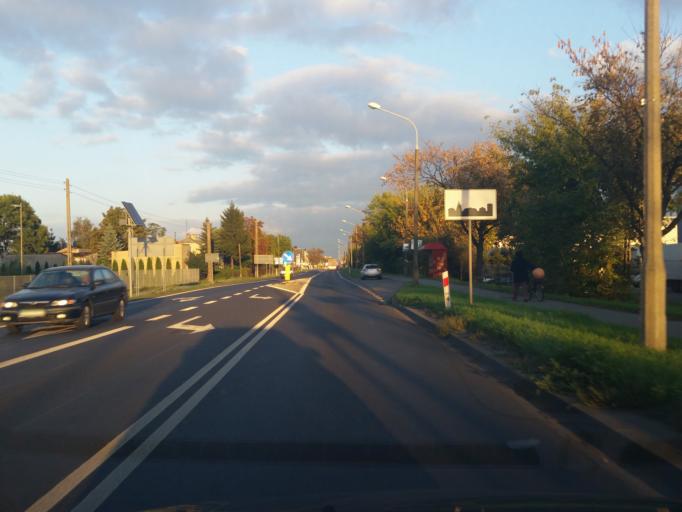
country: PL
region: Masovian Voivodeship
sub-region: Powiat warszawski zachodni
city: Ozarow Mazowiecki
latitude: 52.2111
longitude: 20.7703
